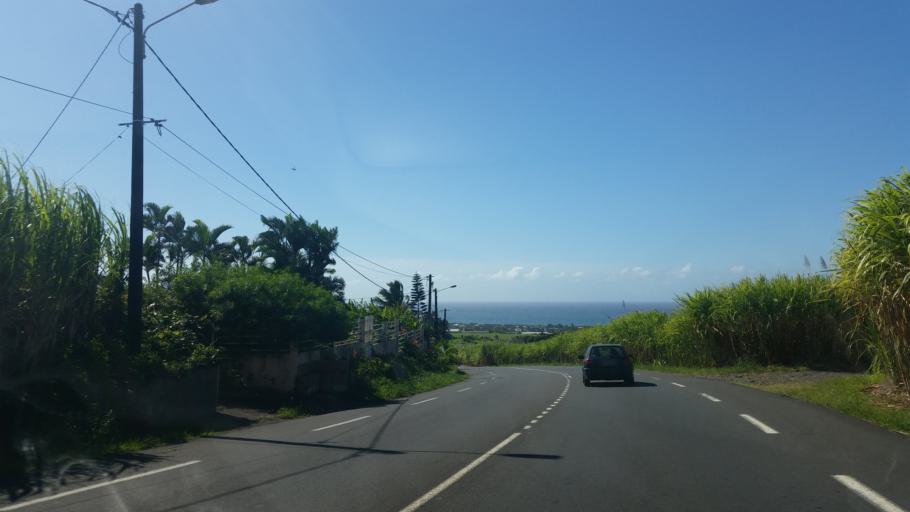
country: RE
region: Reunion
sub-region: Reunion
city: Saint-Benoit
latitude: -21.0654
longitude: 55.7076
